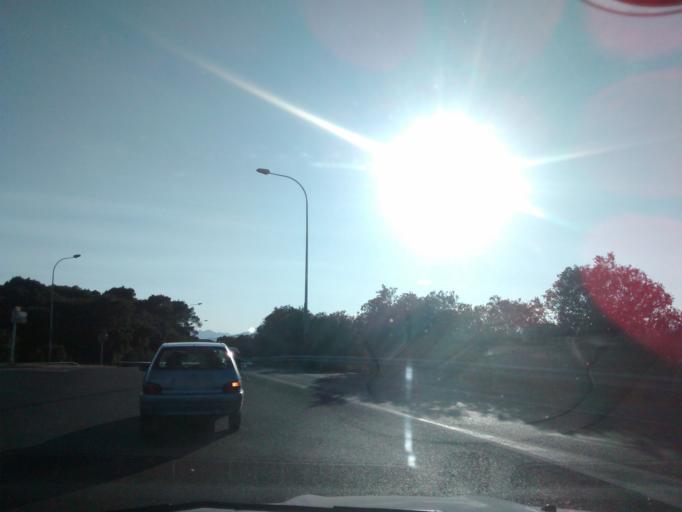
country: ES
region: Balearic Islands
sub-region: Illes Balears
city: Alcudia
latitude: 39.8447
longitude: 3.0937
